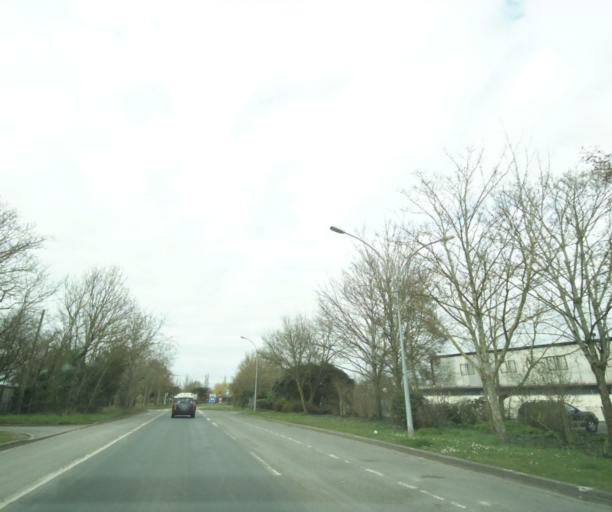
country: FR
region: Poitou-Charentes
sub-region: Departement de la Charente-Maritime
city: La Rochelle
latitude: 46.1731
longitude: -1.1743
